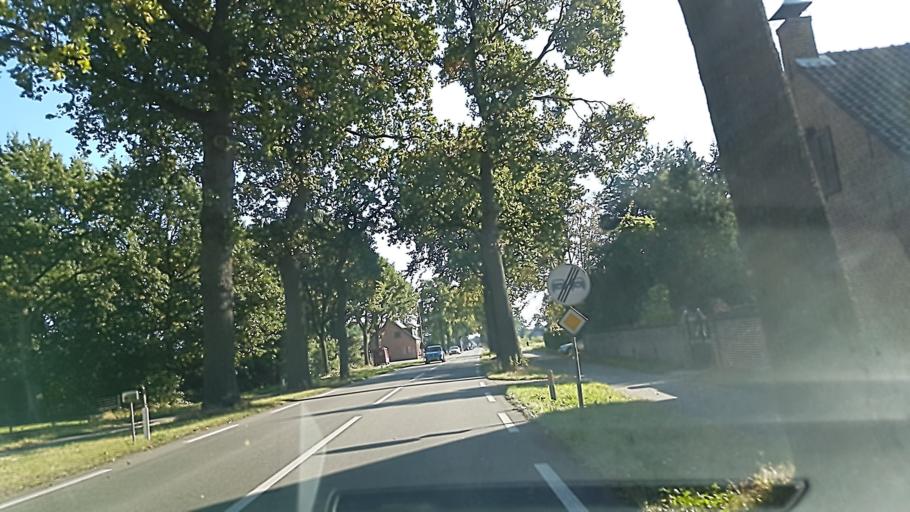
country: BE
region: Flanders
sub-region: Provincie Antwerpen
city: Stabroek
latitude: 51.3703
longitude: 4.3865
